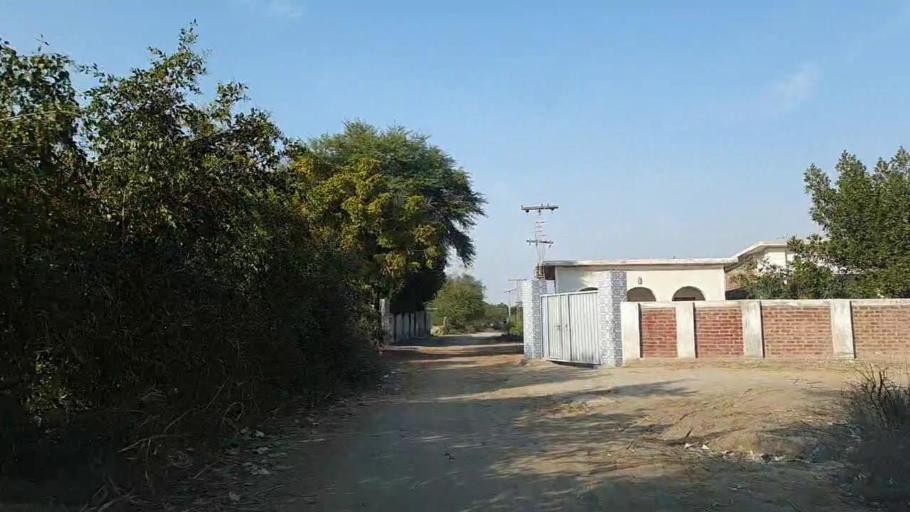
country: PK
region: Sindh
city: Nawabshah
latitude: 26.3821
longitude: 68.4851
